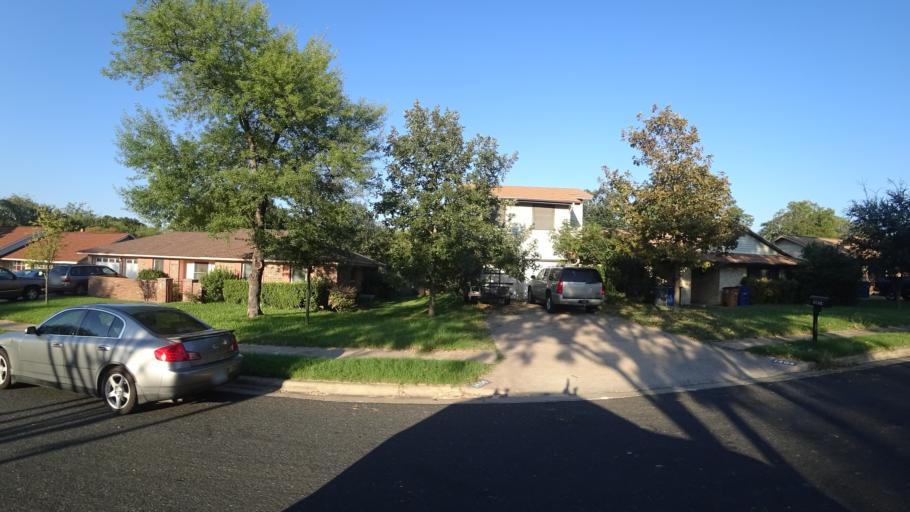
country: US
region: Texas
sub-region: Travis County
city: Wells Branch
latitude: 30.3595
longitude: -97.6720
